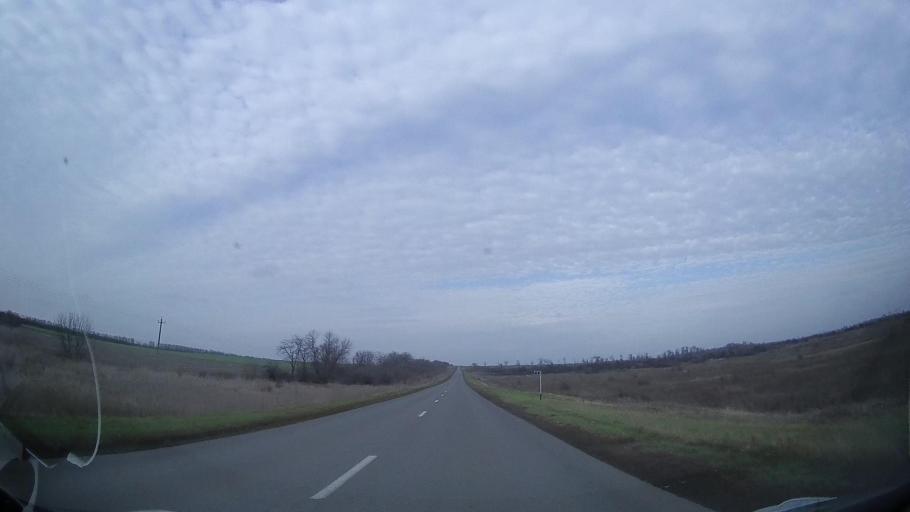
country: RU
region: Rostov
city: Zernograd
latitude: 46.8981
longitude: 40.3389
